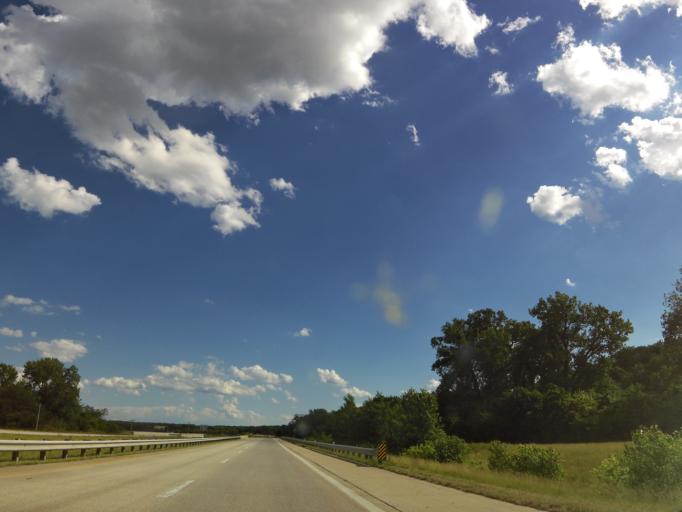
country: US
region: Missouri
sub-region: Clark County
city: Kahoka
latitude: 40.3451
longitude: -91.5870
